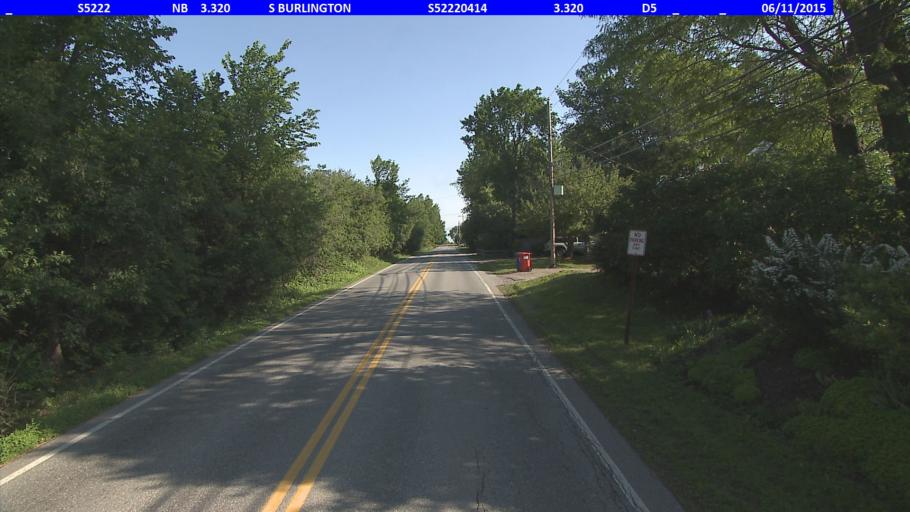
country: US
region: Vermont
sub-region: Chittenden County
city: South Burlington
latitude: 44.4645
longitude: -73.1910
